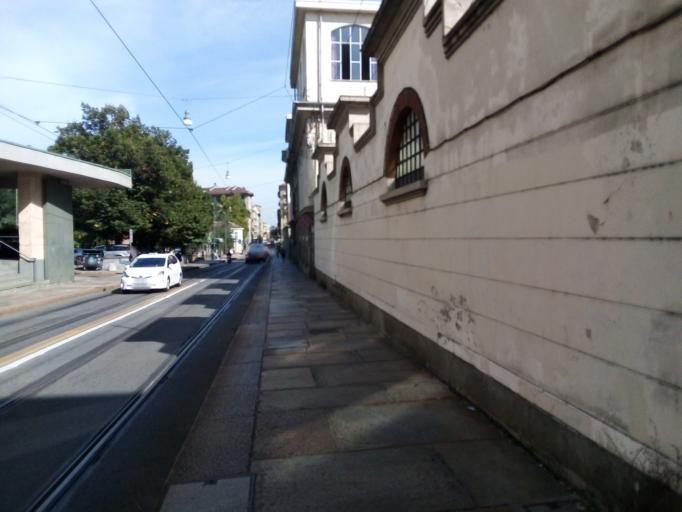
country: IT
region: Piedmont
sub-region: Provincia di Torino
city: Turin
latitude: 45.0702
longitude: 7.6916
